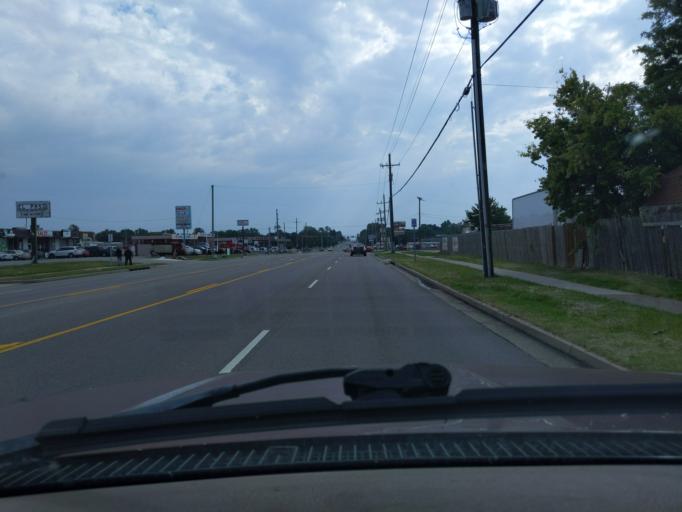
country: US
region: Oklahoma
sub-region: Tulsa County
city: Broken Arrow
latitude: 36.1355
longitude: -95.8333
